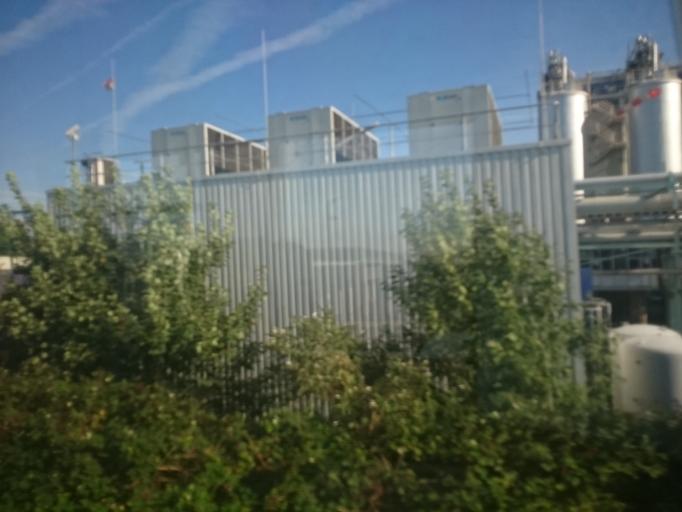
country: DE
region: North Rhine-Westphalia
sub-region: Regierungsbezirk Dusseldorf
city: Dusseldorf
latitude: 51.2246
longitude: 6.8221
